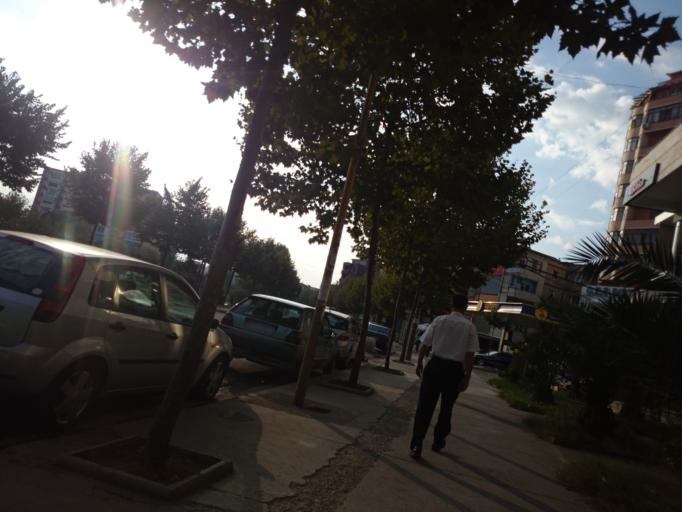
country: AL
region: Tirane
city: Tirana
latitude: 41.3215
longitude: 19.7923
